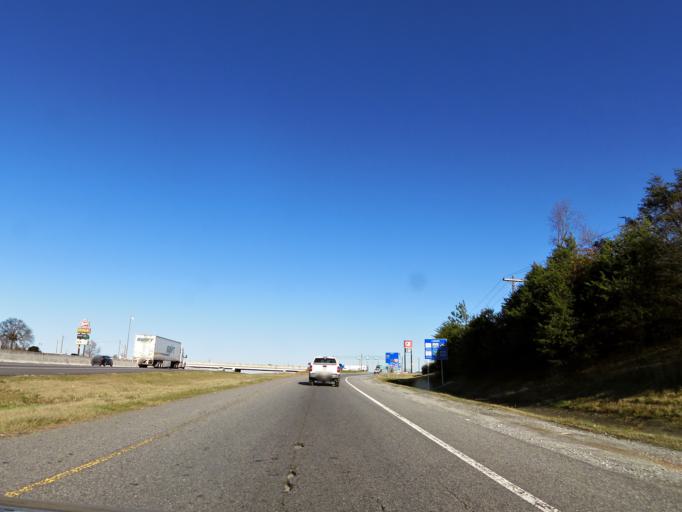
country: US
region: South Carolina
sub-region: Spartanburg County
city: Wellford
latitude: 34.9121
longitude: -82.1099
